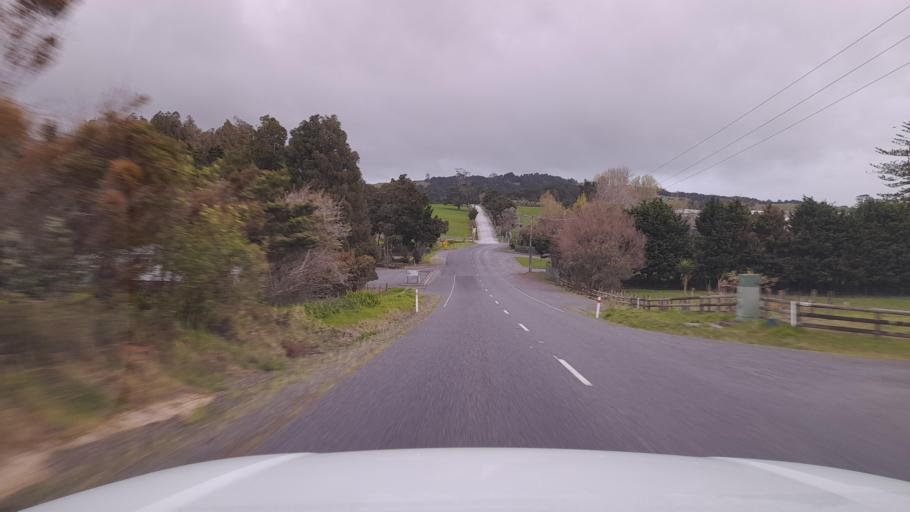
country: NZ
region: Northland
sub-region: Whangarei
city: Maungatapere
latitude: -35.6592
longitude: 174.2233
